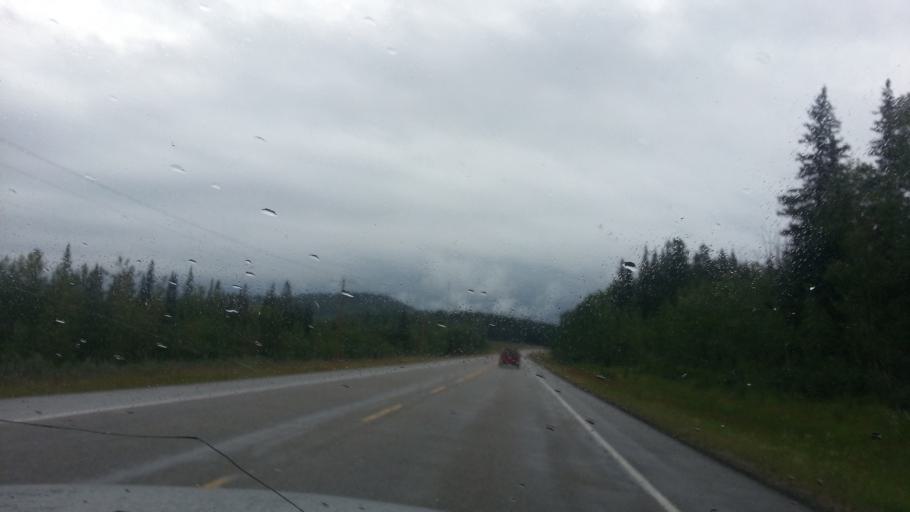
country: CA
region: Alberta
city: Cochrane
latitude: 50.9187
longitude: -114.6083
